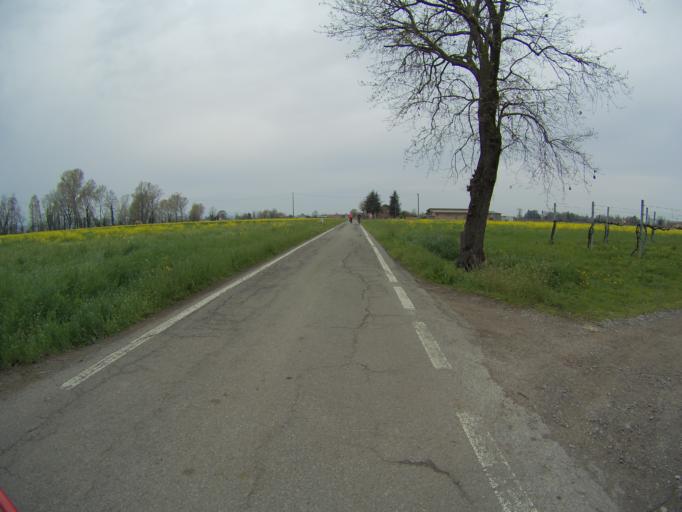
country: IT
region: Emilia-Romagna
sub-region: Provincia di Reggio Emilia
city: Bibbiano
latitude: 44.6614
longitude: 10.4569
